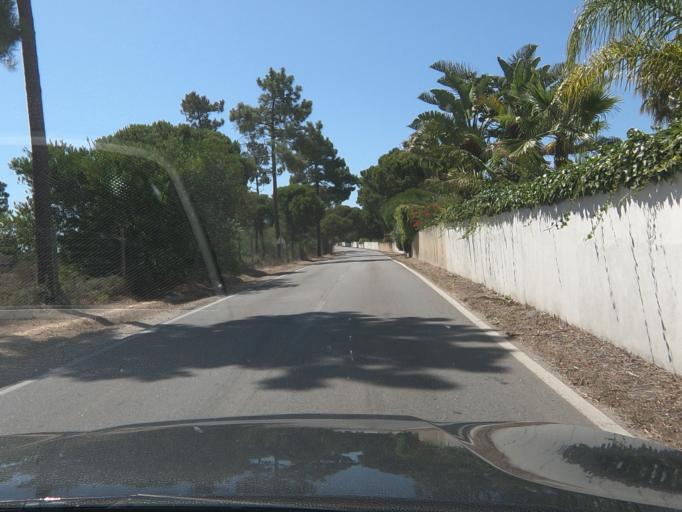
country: PT
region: Faro
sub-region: Loule
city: Vilamoura
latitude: 37.0835
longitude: -8.1003
